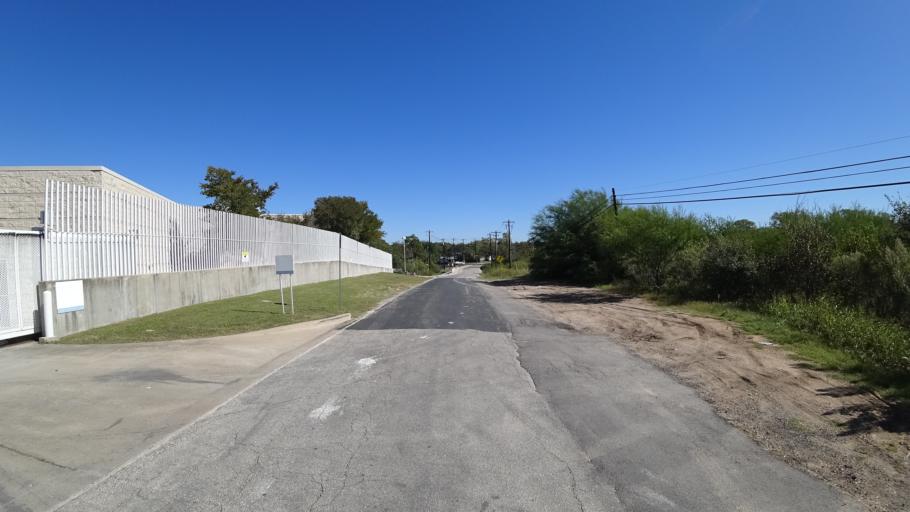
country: US
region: Texas
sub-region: Travis County
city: Austin
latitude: 30.2986
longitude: -97.6912
